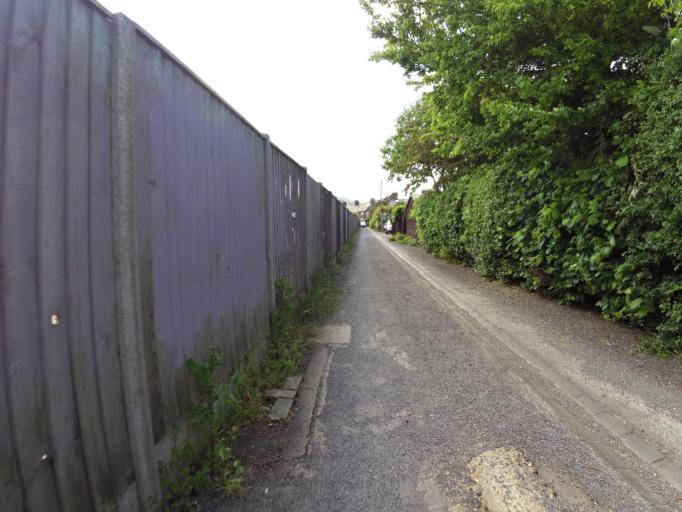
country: GB
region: England
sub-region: Norfolk
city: Thorpe Hamlet
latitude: 52.6227
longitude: 1.3151
